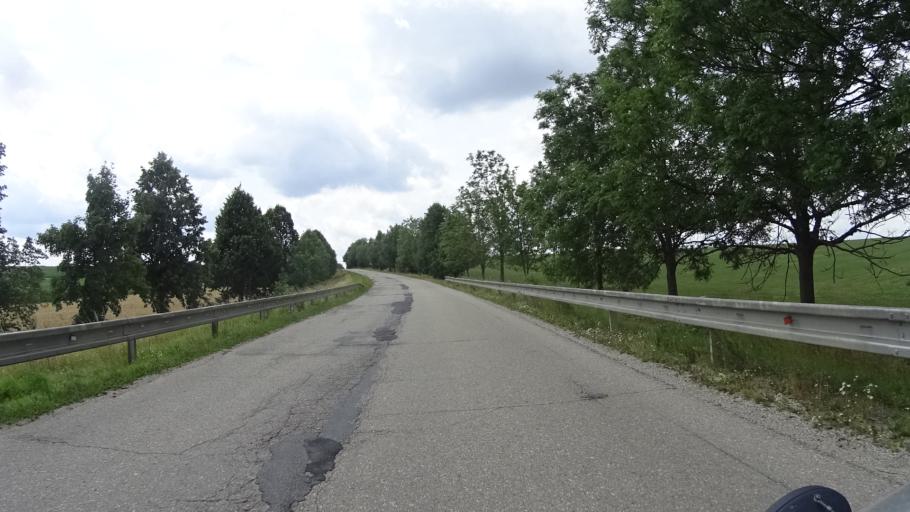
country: CZ
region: Vysocina
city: Merin
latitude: 49.3972
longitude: 15.9016
